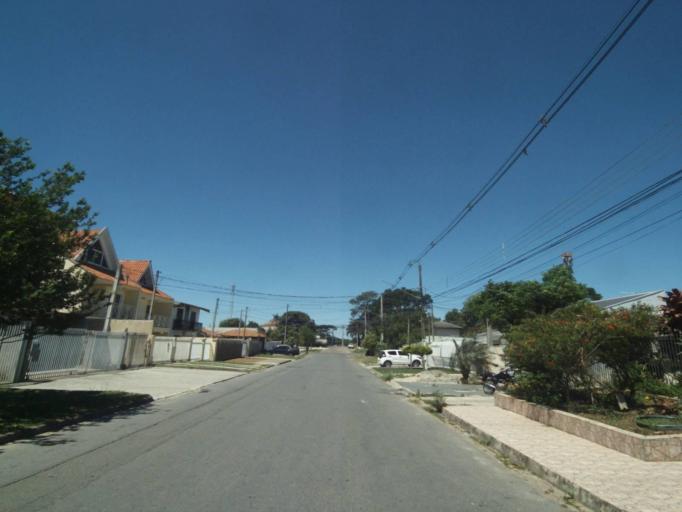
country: BR
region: Parana
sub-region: Curitiba
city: Curitiba
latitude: -25.4810
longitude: -49.3447
